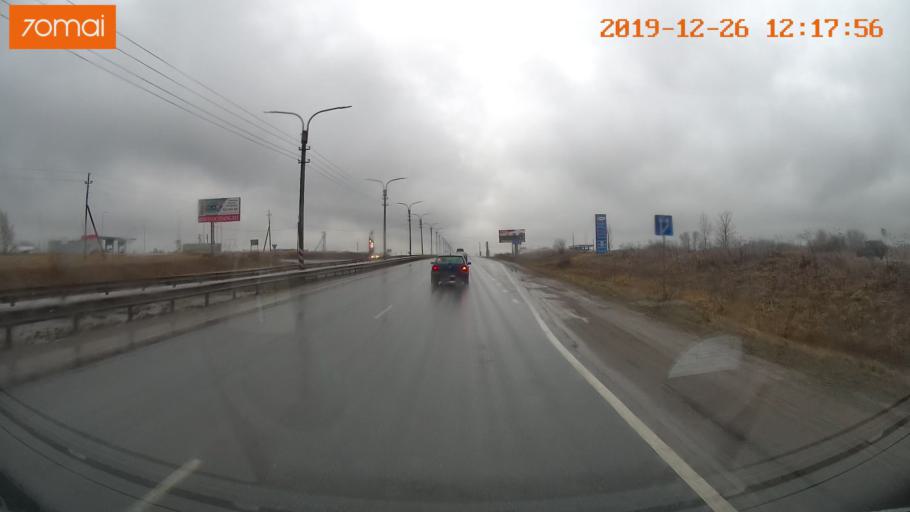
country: RU
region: Vologda
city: Tonshalovo
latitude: 59.1841
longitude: 37.9436
